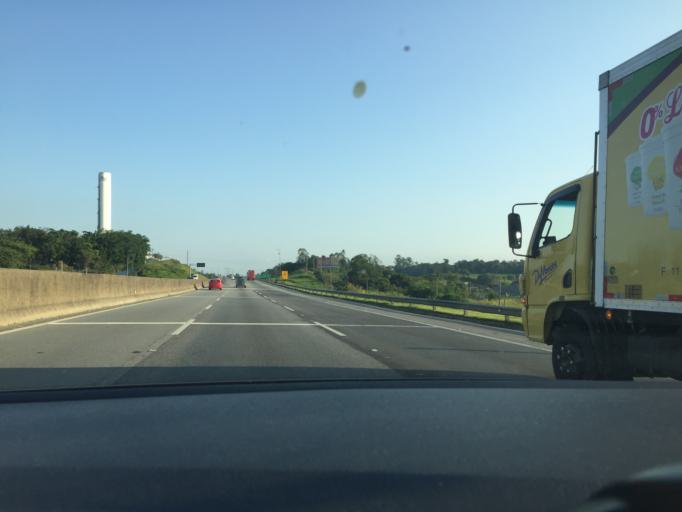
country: BR
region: Sao Paulo
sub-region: Louveira
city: Louveira
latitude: -23.1056
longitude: -46.9628
